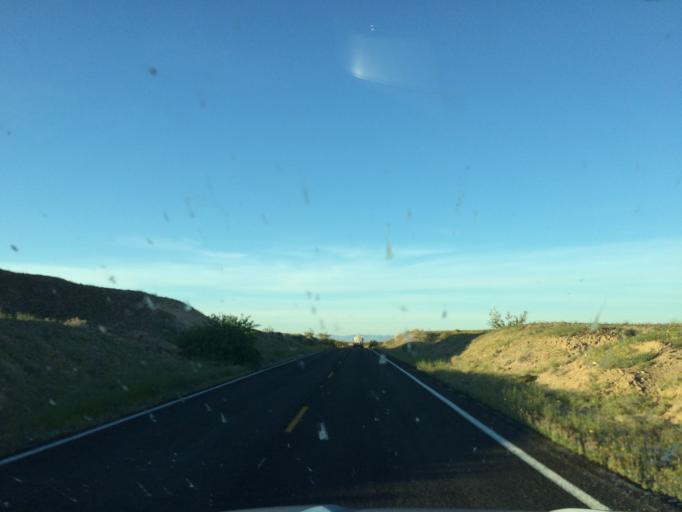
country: US
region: California
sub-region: Riverside County
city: Mesa Verde
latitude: 33.3471
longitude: -114.7231
